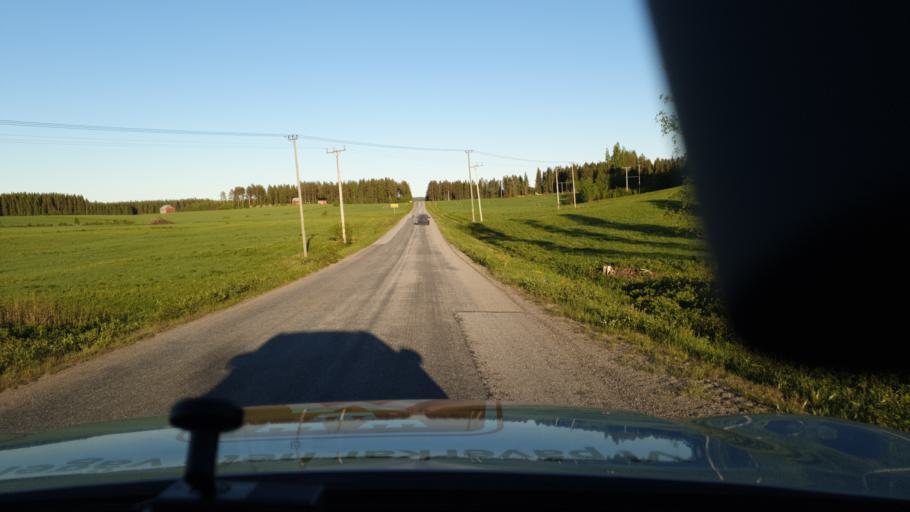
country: SE
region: Vaesterbotten
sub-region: Umea Kommun
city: Roback
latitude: 64.0249
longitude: 20.0902
